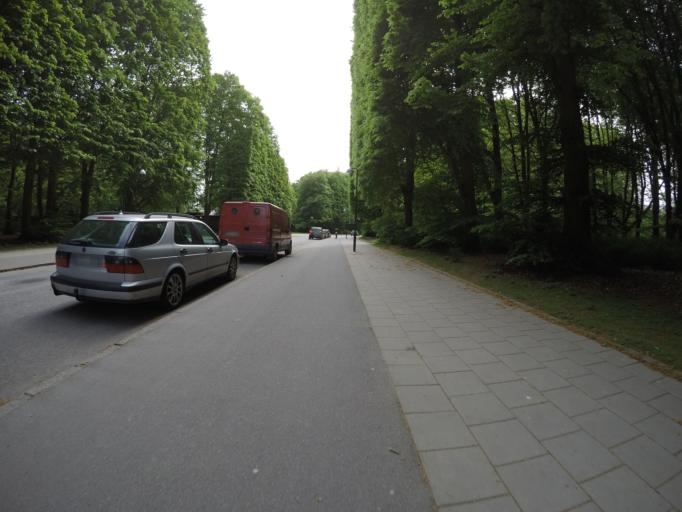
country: SE
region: Skane
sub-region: Malmo
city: Malmoe
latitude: 55.5904
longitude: 12.9912
